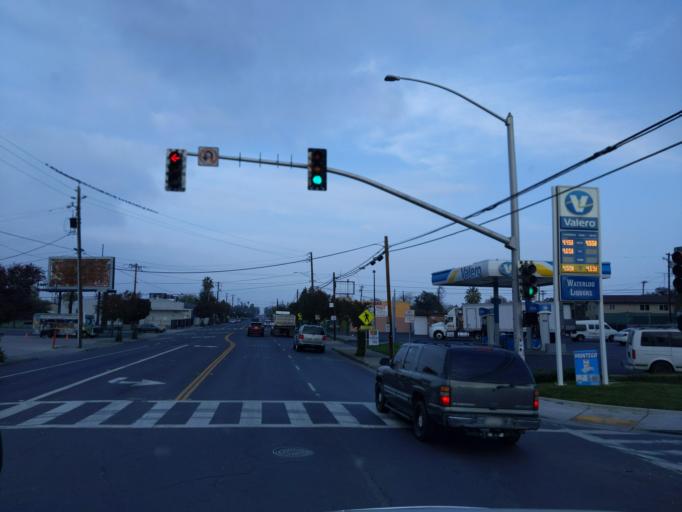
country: US
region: California
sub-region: San Joaquin County
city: August
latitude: 37.9770
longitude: -121.2619
